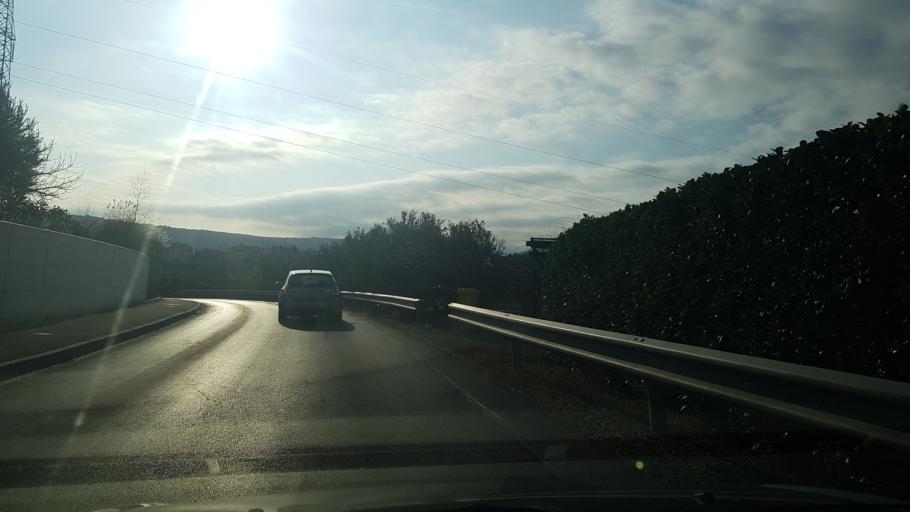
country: SI
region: Koper-Capodistria
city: Prade
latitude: 45.5374
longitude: 13.7729
